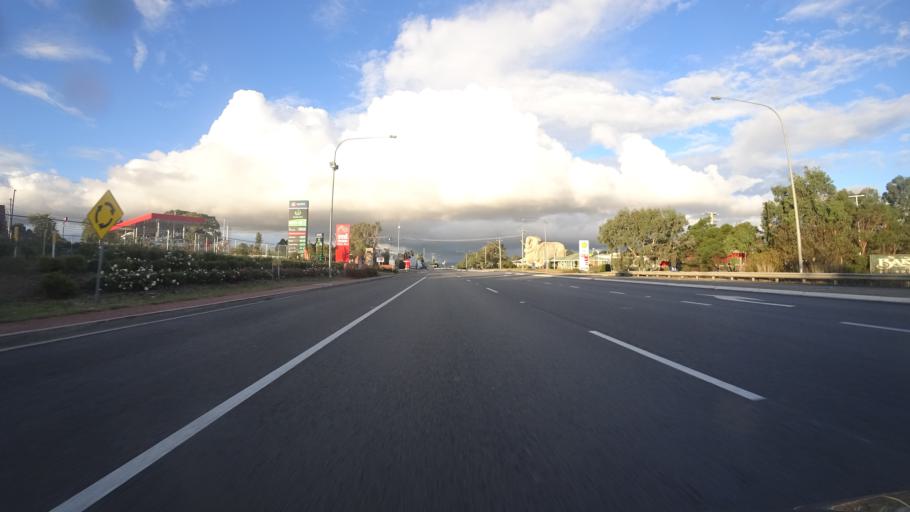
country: AU
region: New South Wales
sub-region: Goulburn Mulwaree
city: Goulburn
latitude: -34.7732
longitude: 149.6898
